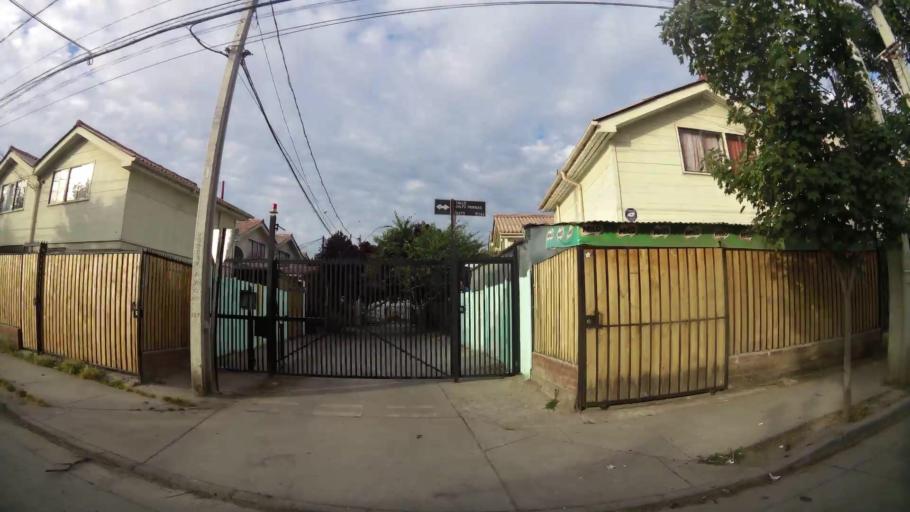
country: CL
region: Santiago Metropolitan
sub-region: Provincia de Maipo
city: San Bernardo
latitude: -33.6456
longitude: -70.6643
